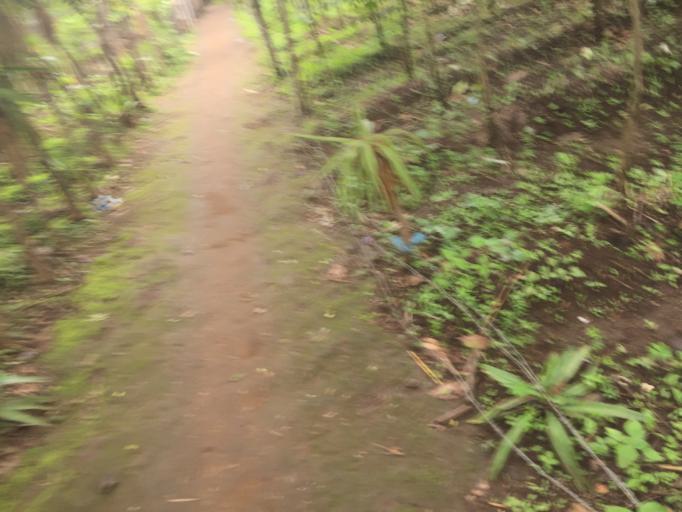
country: GT
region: Sacatepequez
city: Magdalena Milpas Altas
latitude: 14.5107
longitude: -90.6518
